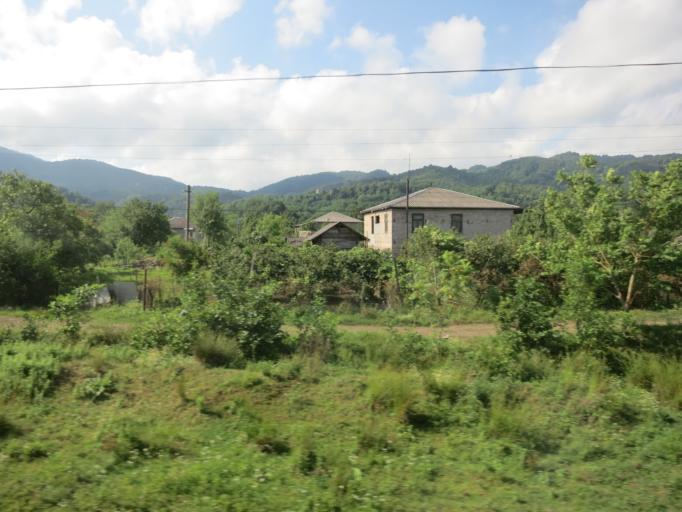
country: GE
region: Guria
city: Lanchkhuti
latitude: 42.0908
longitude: 42.1416
